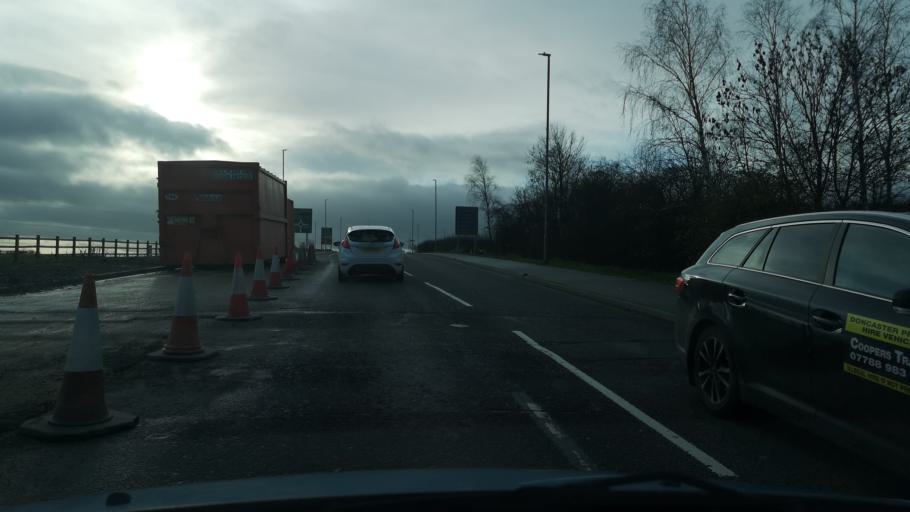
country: GB
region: England
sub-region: Barnsley
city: Little Houghton
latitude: 53.5360
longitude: -1.3538
